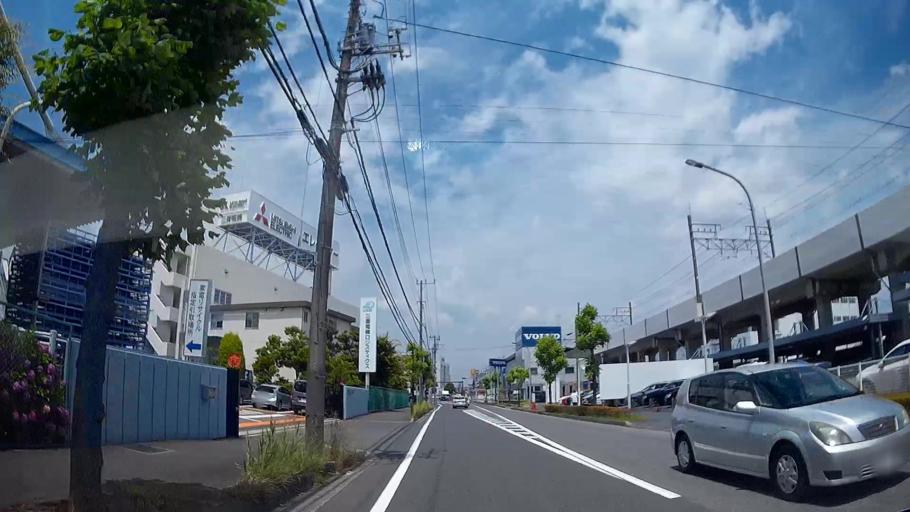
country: JP
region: Tokyo
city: Urayasu
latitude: 35.6648
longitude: 139.9225
